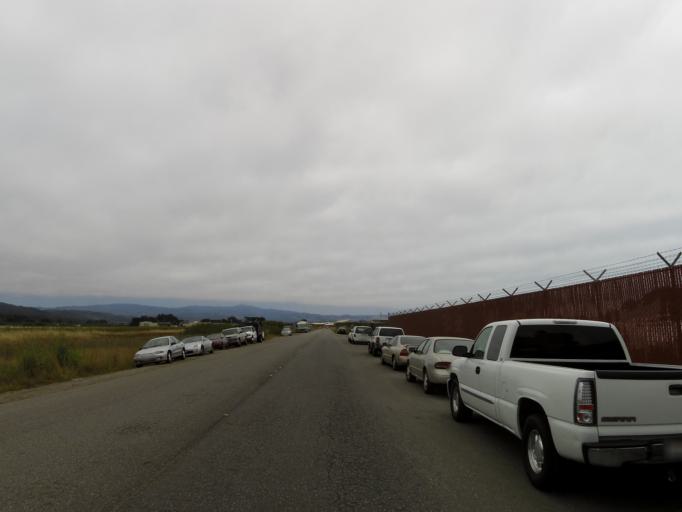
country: US
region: California
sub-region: San Mateo County
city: Moss Beach
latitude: 37.5094
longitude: -122.4981
